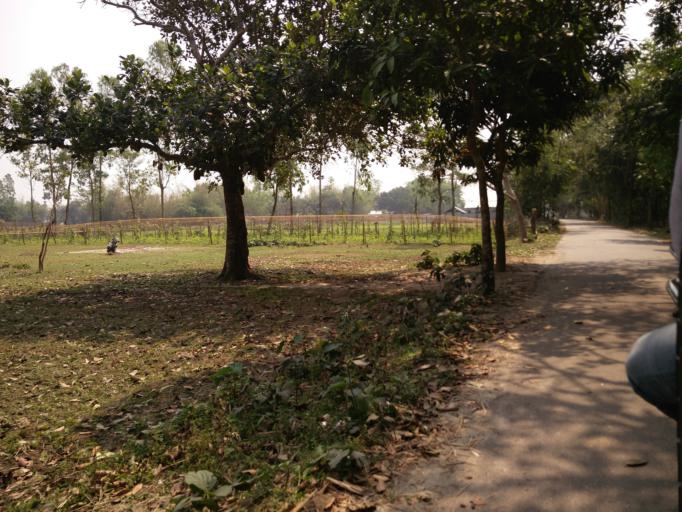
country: BD
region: Dhaka
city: Muktagacha
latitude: 24.8911
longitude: 90.2675
